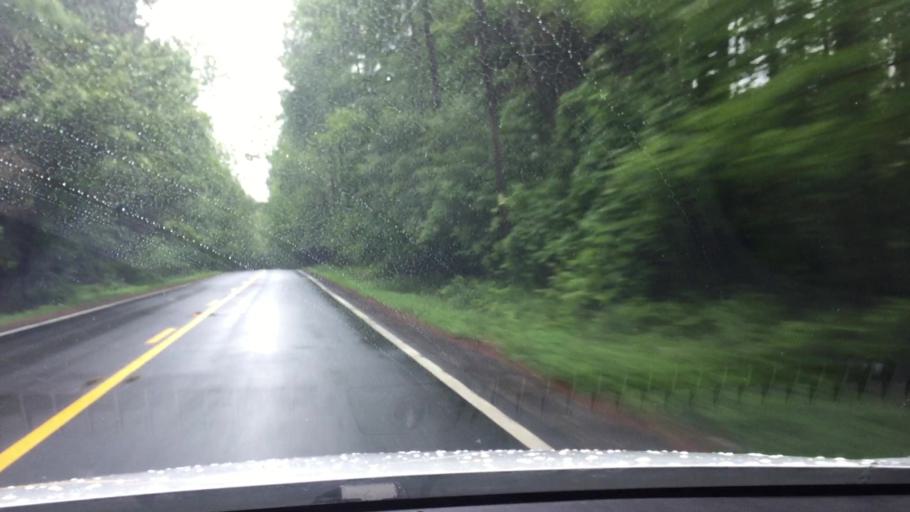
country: US
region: Massachusetts
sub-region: Berkshire County
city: Hinsdale
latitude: 42.4016
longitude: -73.1731
